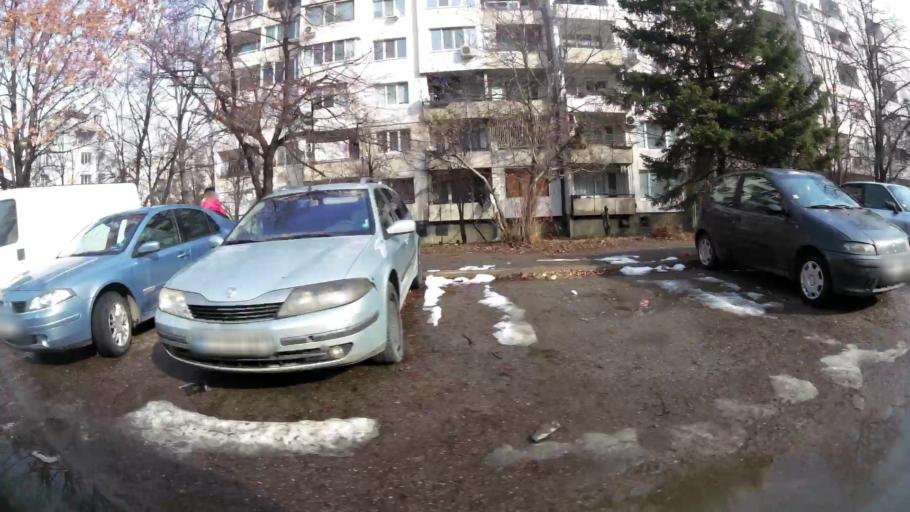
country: BG
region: Sofia-Capital
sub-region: Stolichna Obshtina
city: Sofia
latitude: 42.7166
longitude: 23.2637
